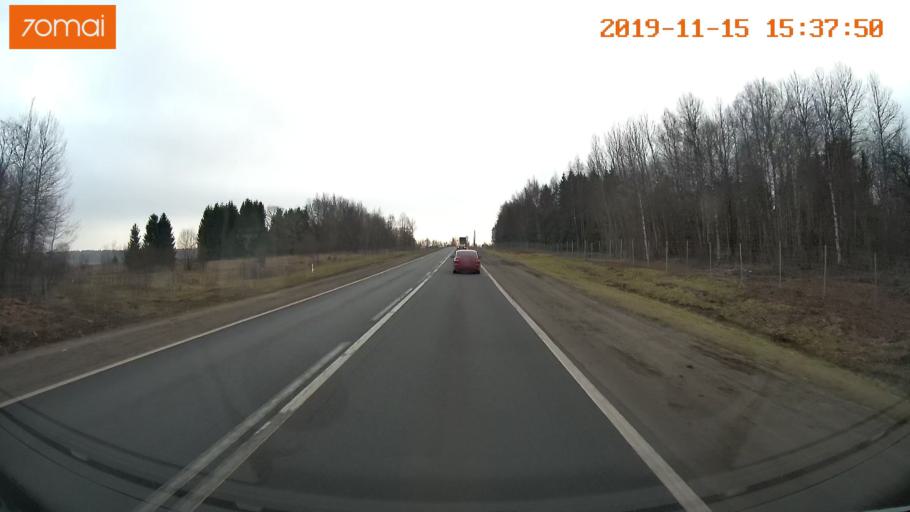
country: RU
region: Jaroslavl
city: Danilov
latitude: 58.0354
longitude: 40.0859
